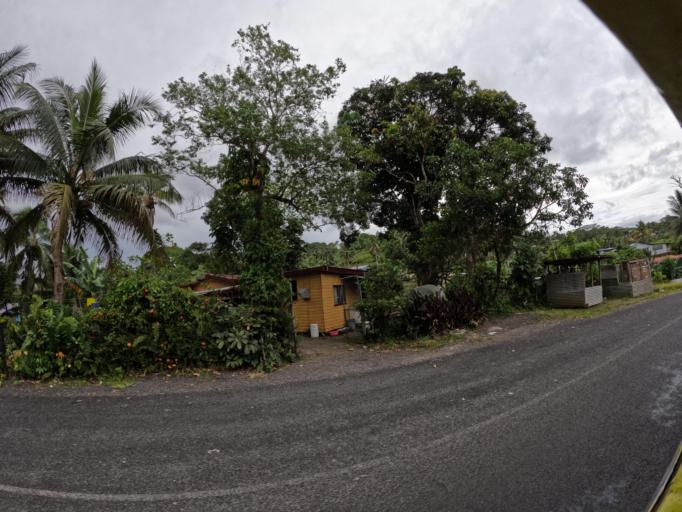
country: FJ
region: Central
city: Suva
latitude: -18.0723
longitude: 178.4613
